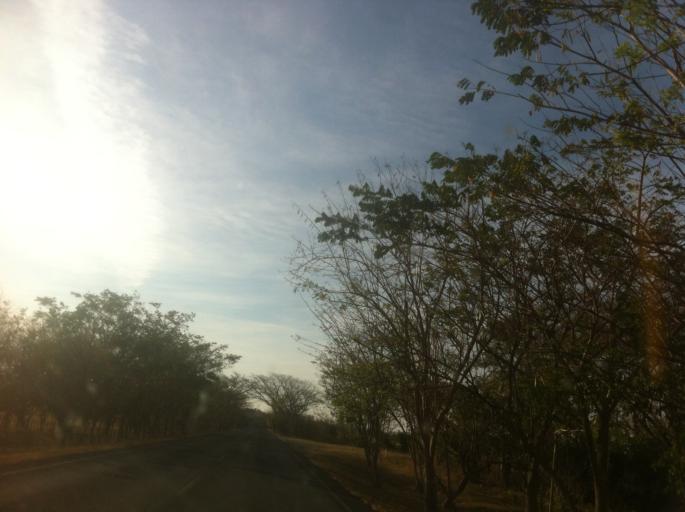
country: NI
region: Rivas
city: San Jorge
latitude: 11.3231
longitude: -85.7138
